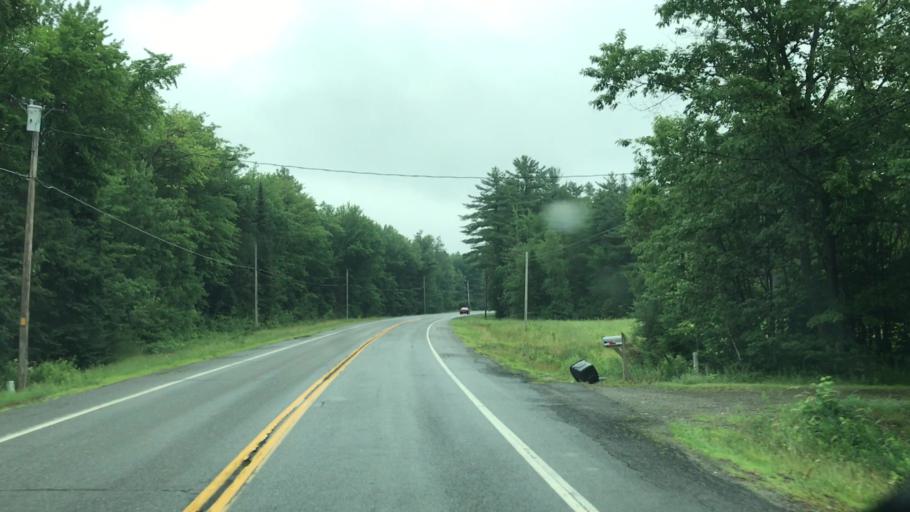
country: US
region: Maine
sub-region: Penobscot County
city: Howland
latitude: 45.2709
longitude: -68.6384
